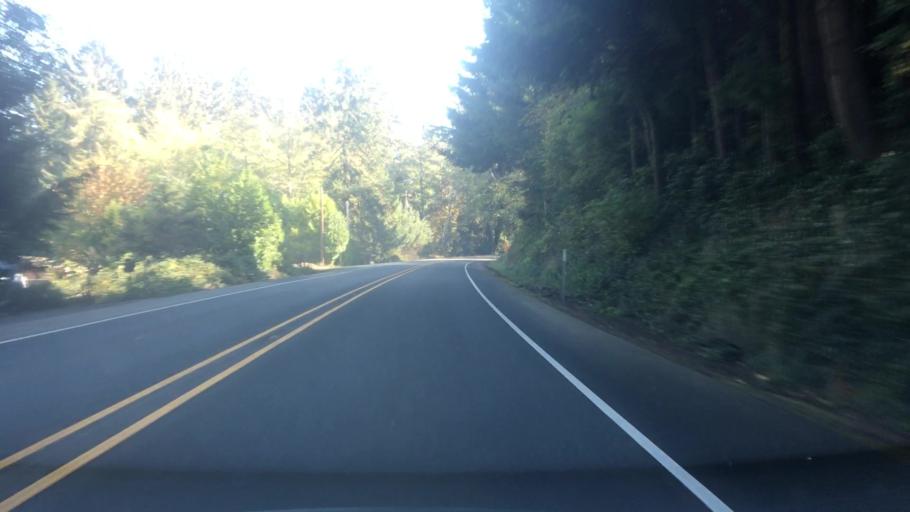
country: US
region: Oregon
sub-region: Lincoln County
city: Rose Lodge
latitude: 45.0059
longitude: -123.9150
